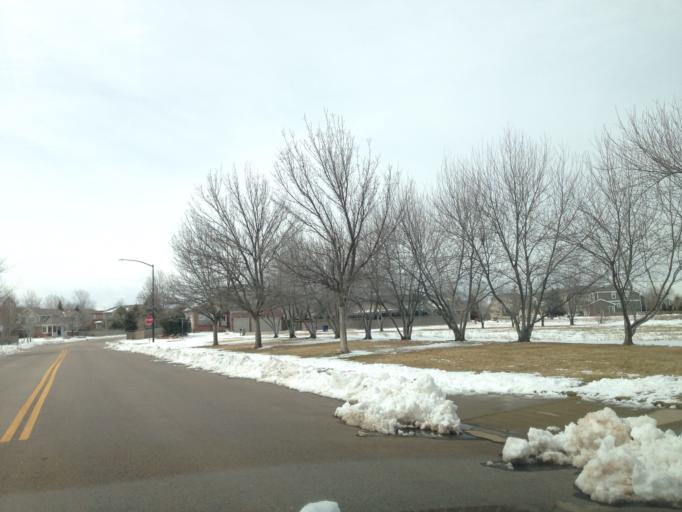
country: US
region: Colorado
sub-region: Boulder County
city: Lafayette
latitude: 39.9673
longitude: -105.0926
